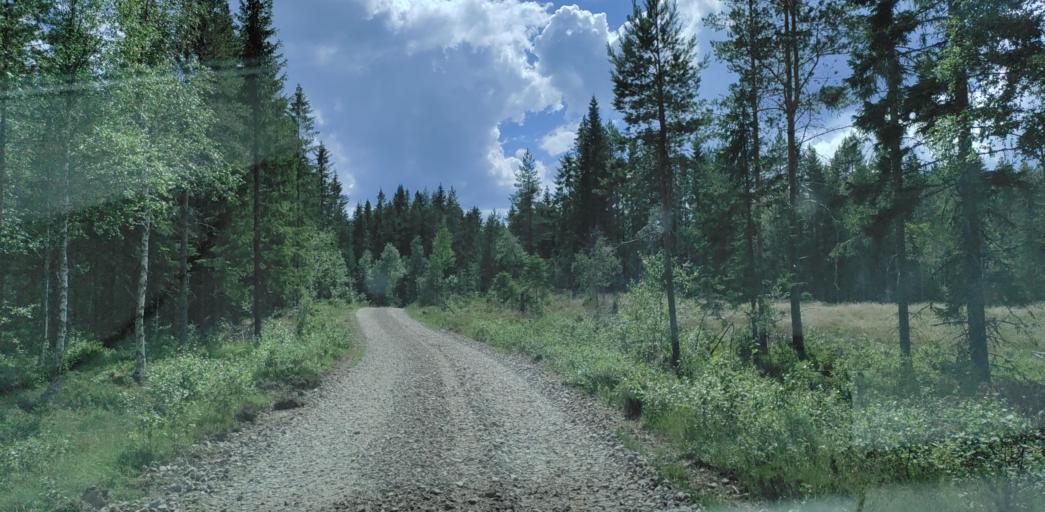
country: SE
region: Vaermland
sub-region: Hagfors Kommun
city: Ekshaerad
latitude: 60.0758
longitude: 13.3458
